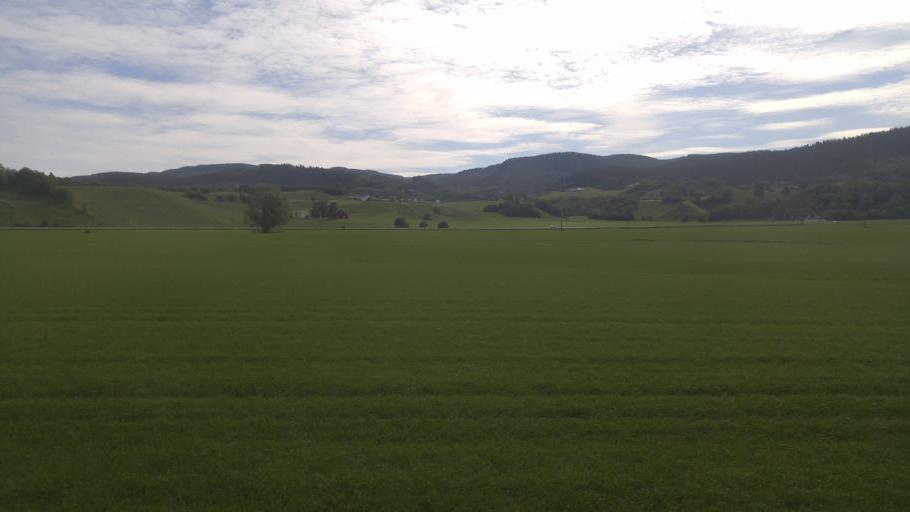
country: NO
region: Sor-Trondelag
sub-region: Melhus
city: Lundamo
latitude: 63.1824
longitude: 10.3082
